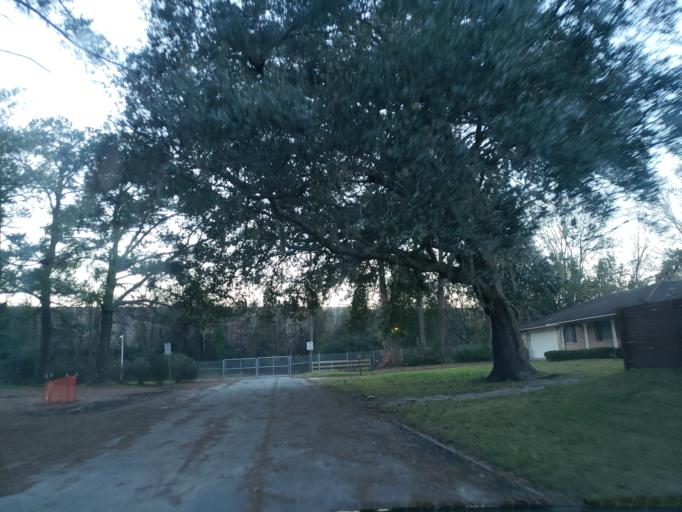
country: US
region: Georgia
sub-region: Chatham County
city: Thunderbolt
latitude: 32.0203
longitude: -81.0875
